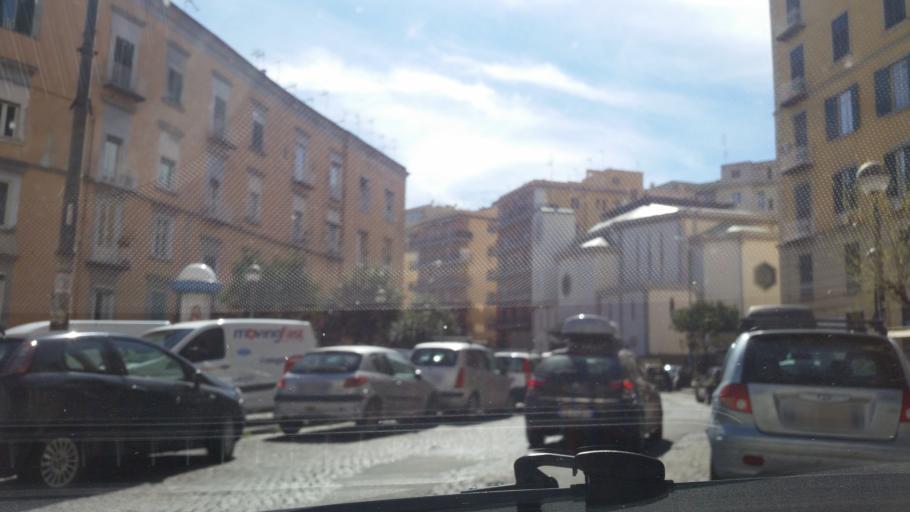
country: IT
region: Campania
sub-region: Provincia di Napoli
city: Napoli
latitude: 40.8540
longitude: 14.2357
